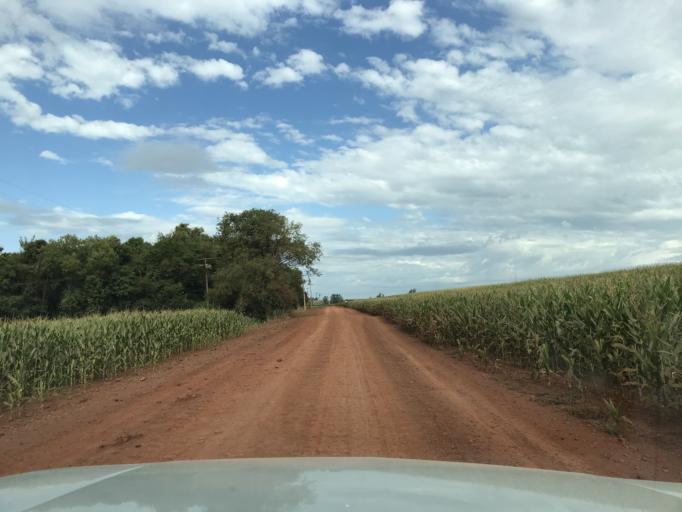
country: BR
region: Parana
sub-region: Palotina
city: Palotina
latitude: -24.3123
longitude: -53.8079
